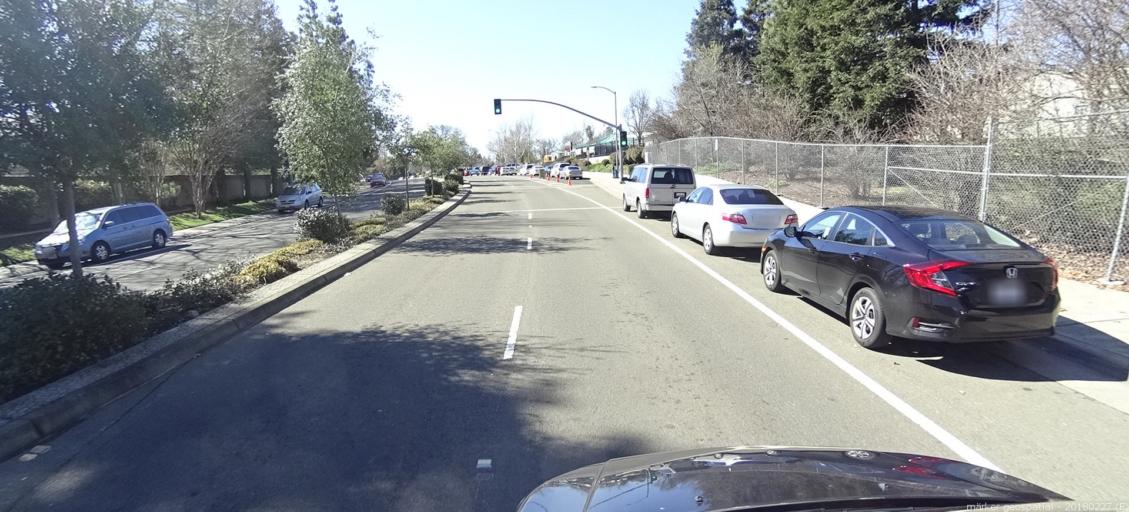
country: US
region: California
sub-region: Sacramento County
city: North Highlands
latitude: 38.7211
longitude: -121.3721
